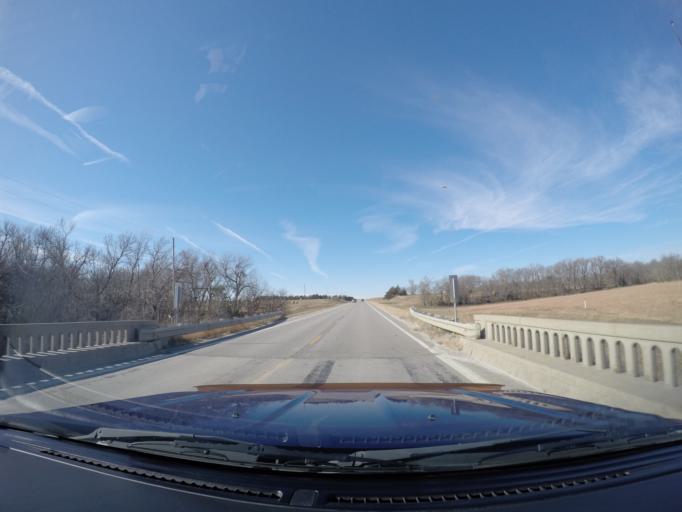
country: US
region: Kansas
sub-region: Cloud County
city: Concordia
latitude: 39.3647
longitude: -97.5751
